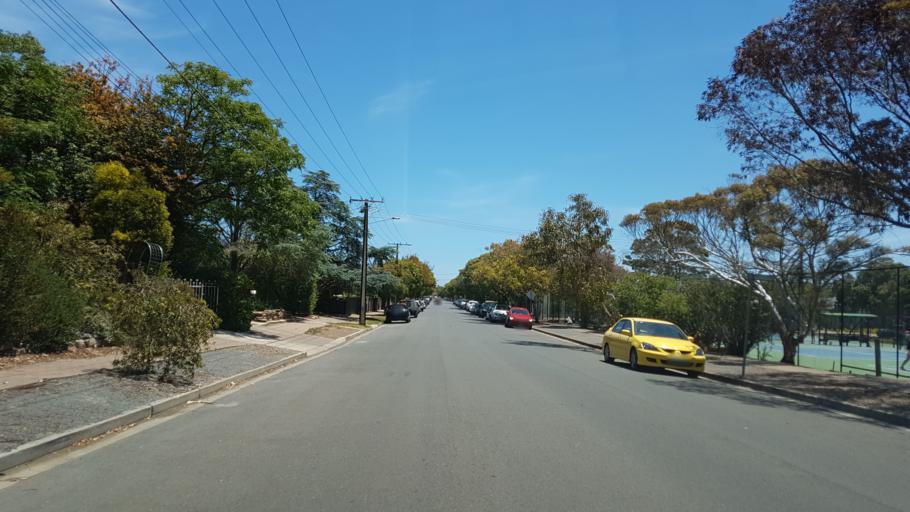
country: AU
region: South Australia
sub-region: Holdfast Bay
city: Seacliff Park
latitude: -35.0259
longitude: 138.5292
